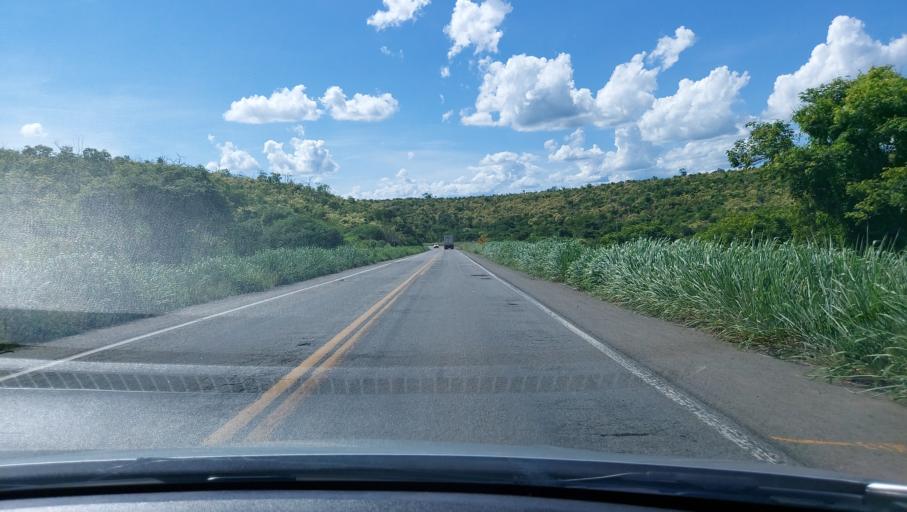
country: BR
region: Bahia
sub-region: Andarai
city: Vera Cruz
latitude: -12.4669
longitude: -41.0813
